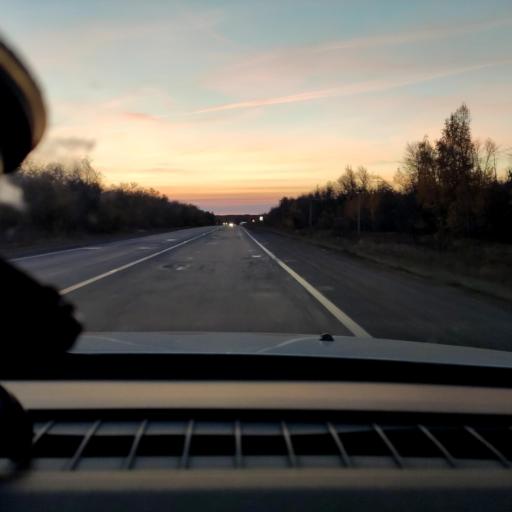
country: RU
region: Samara
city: Novokuybyshevsk
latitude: 52.9864
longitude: 49.8646
